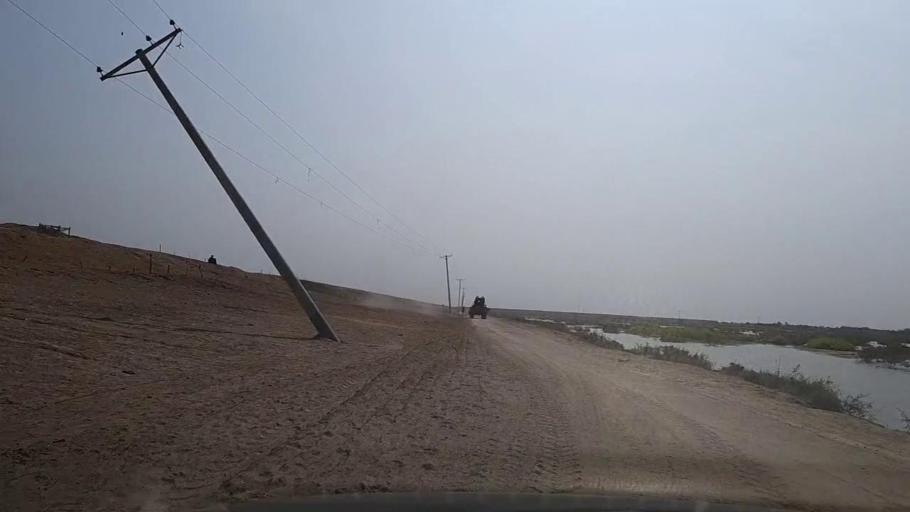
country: PK
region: Sindh
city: Thatta
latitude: 24.5786
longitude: 67.9154
